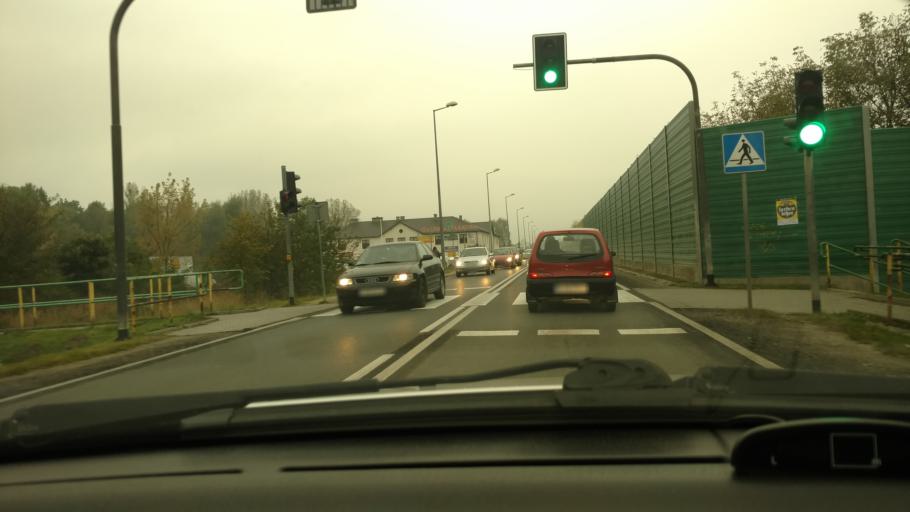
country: PL
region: Lesser Poland Voivodeship
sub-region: Powiat gorlicki
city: Gorlice
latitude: 49.6593
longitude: 21.1657
